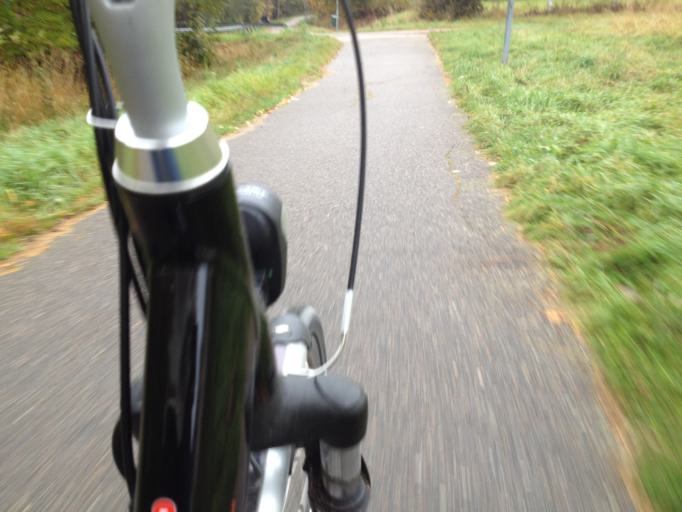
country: SE
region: Gaevleborg
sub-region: Bollnas Kommun
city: Bollnas
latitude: 61.3470
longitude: 16.3831
